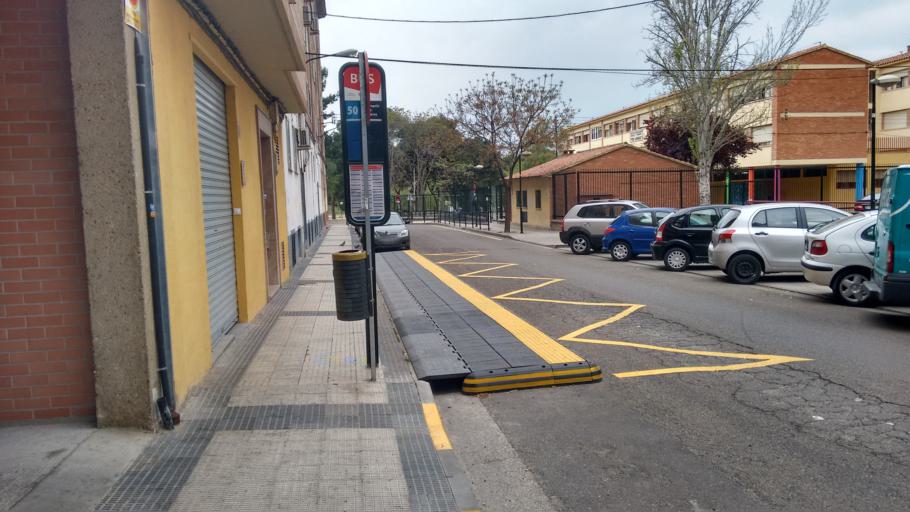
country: ES
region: Aragon
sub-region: Provincia de Zaragoza
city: Zaragoza
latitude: 41.6621
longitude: -0.8748
